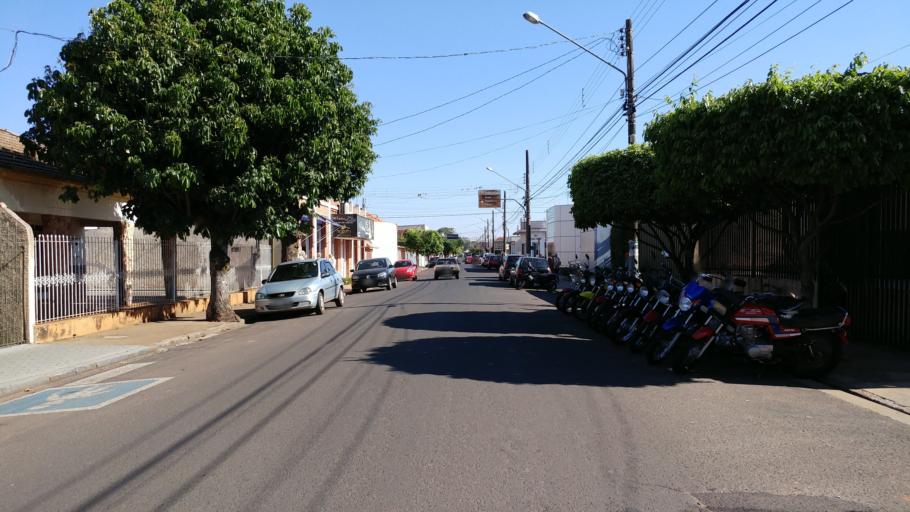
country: BR
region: Sao Paulo
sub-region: Paraguacu Paulista
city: Paraguacu Paulista
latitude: -22.4169
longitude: -50.5751
